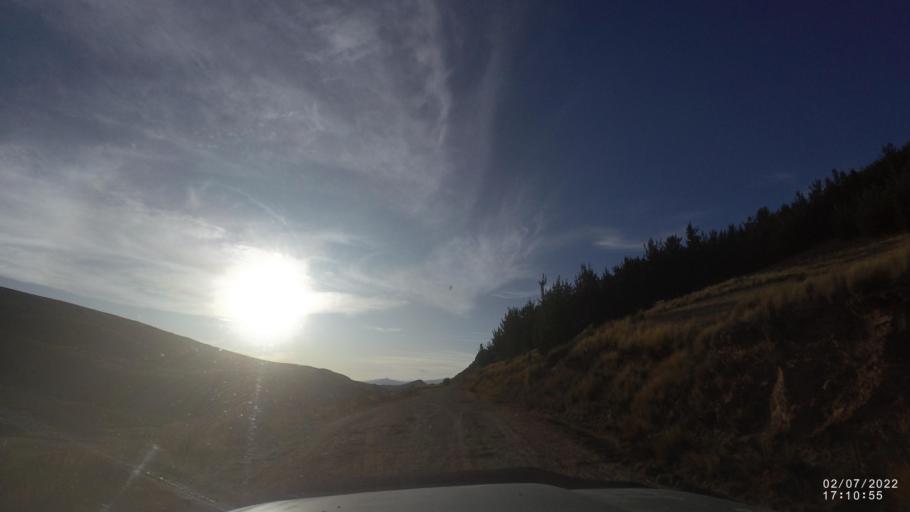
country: BO
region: Cochabamba
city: Irpa Irpa
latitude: -17.8939
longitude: -66.5621
